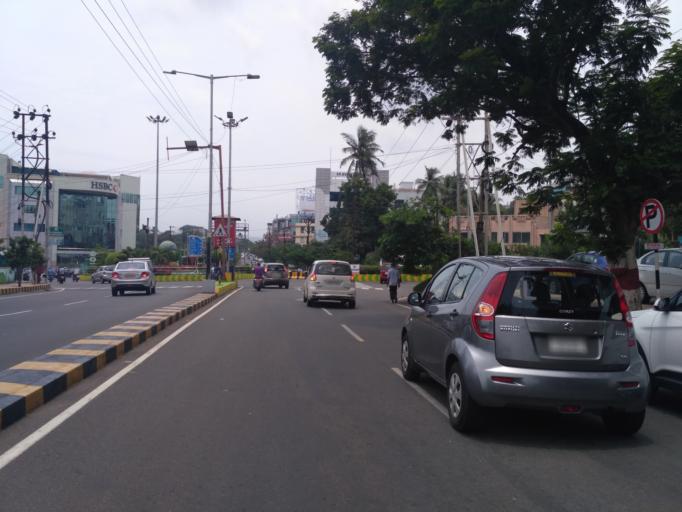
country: IN
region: Andhra Pradesh
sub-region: Vishakhapatnam
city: Yarada
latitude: 17.7236
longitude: 83.3184
